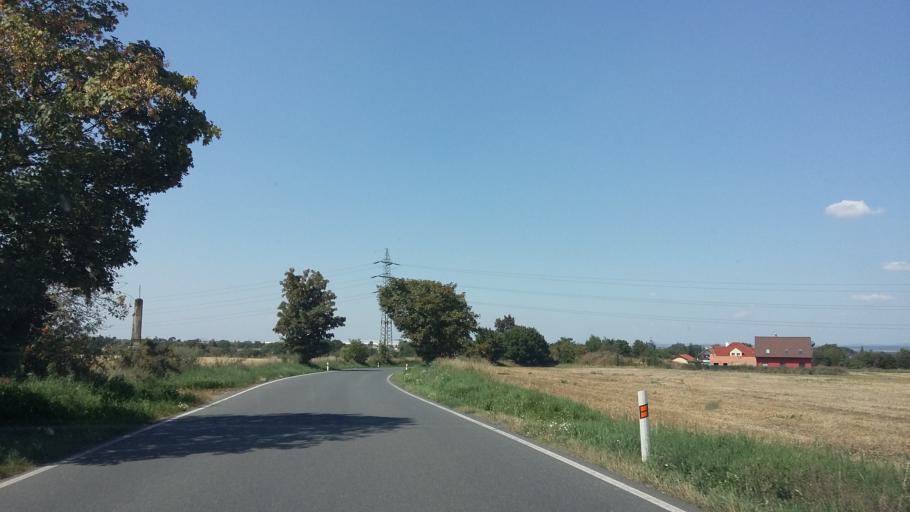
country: CZ
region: Central Bohemia
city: Zelenec
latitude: 50.1586
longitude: 14.6826
